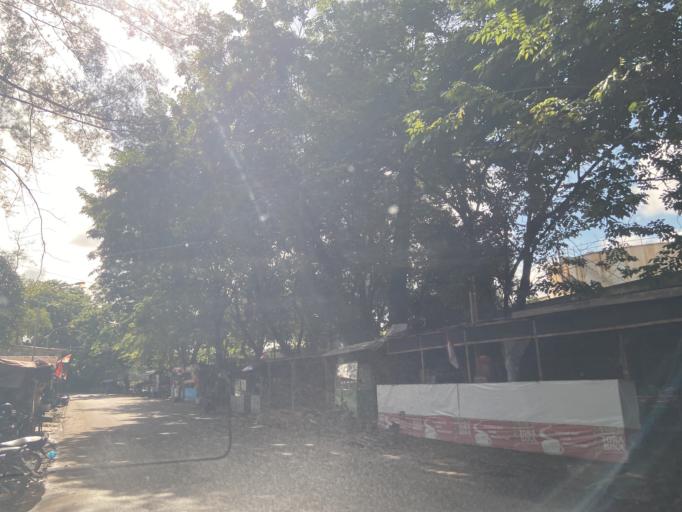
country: SG
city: Singapore
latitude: 1.1690
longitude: 104.0072
